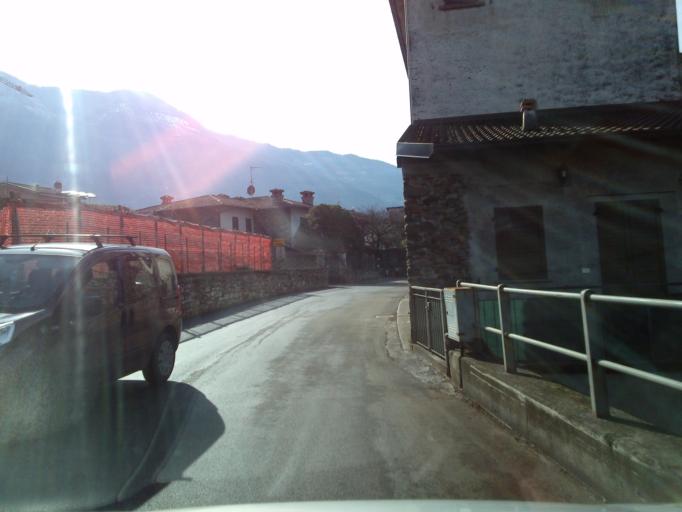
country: IT
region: Lombardy
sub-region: Provincia di Lecco
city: Colico Piano
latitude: 46.1323
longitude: 9.3790
